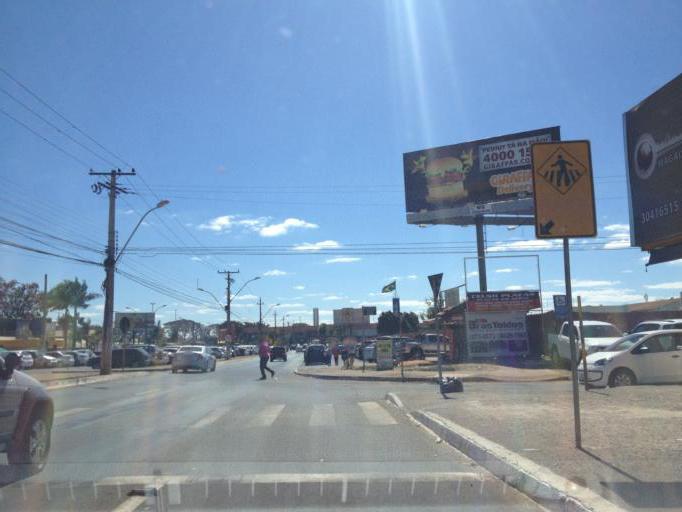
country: BR
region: Federal District
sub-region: Brasilia
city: Brasilia
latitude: -15.7976
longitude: -47.9493
